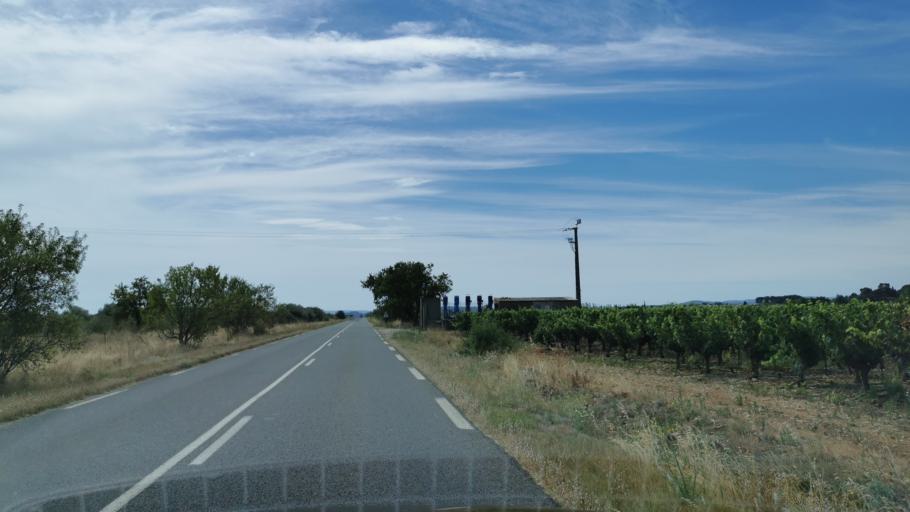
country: FR
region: Languedoc-Roussillon
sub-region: Departement de l'Aude
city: Ginestas
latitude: 43.2856
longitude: 2.8721
